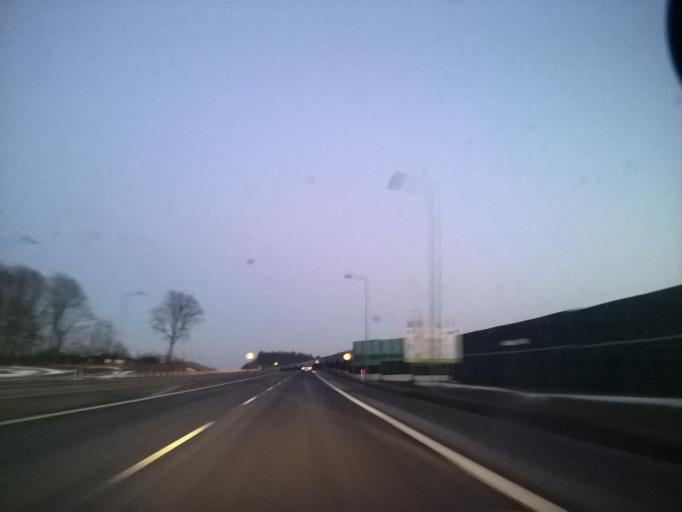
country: PL
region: Warmian-Masurian Voivodeship
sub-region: Powiat olsztynski
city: Biskupiec
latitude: 53.8479
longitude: 20.9769
